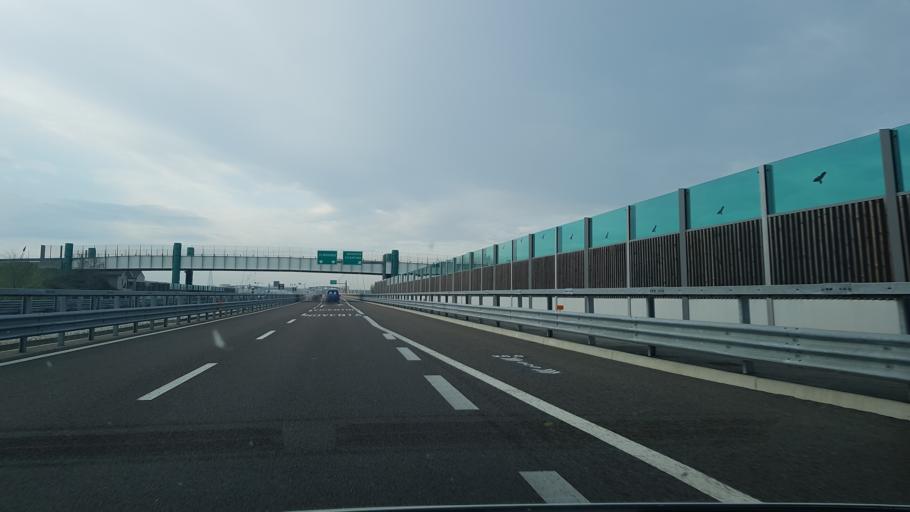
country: IT
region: Veneto
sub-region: Provincia di Vicenza
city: Noventa Vicentina
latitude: 45.2835
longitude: 11.5722
